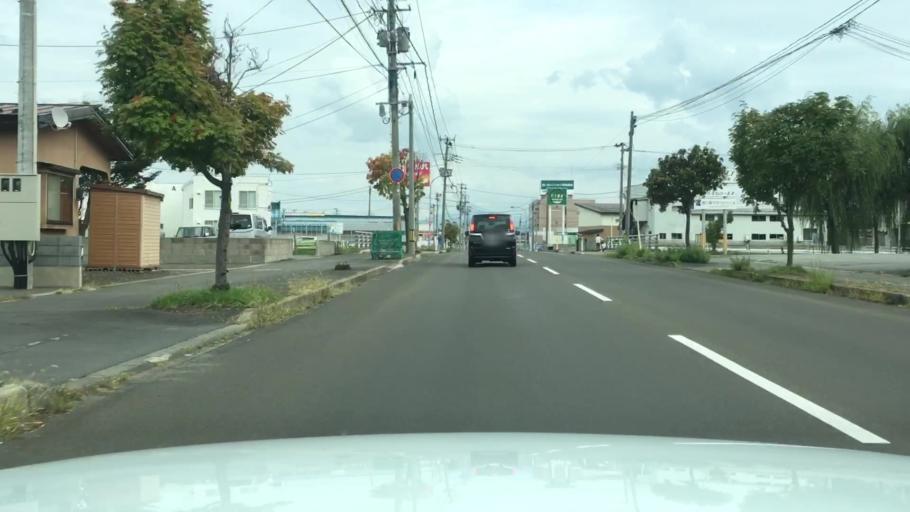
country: JP
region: Aomori
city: Hirosaki
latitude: 40.6160
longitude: 140.4879
